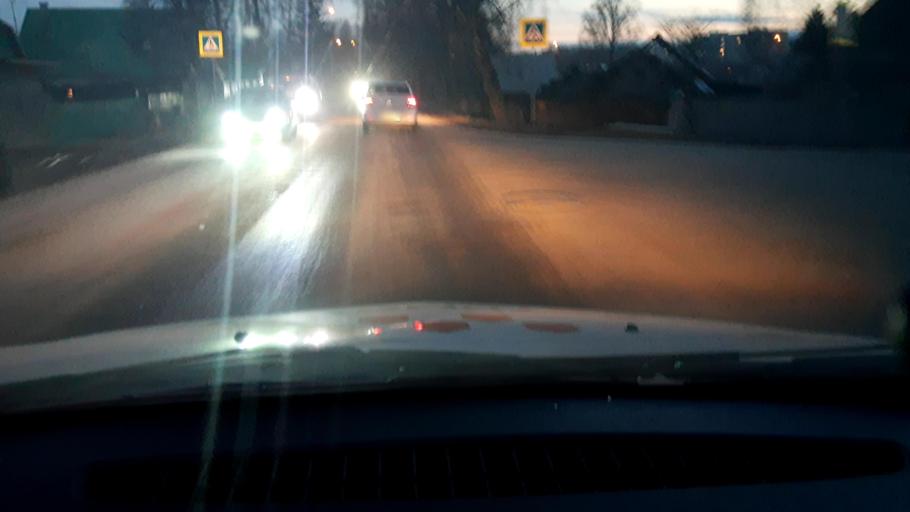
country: RU
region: Bashkortostan
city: Iglino
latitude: 54.7749
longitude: 56.2277
